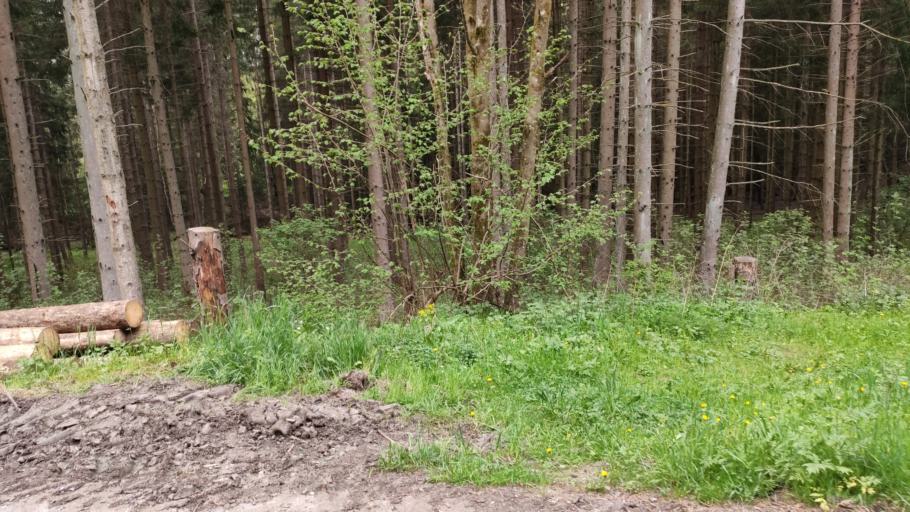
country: DE
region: Bavaria
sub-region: Upper Franconia
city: Ludwigsstadt
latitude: 50.4694
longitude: 11.4157
